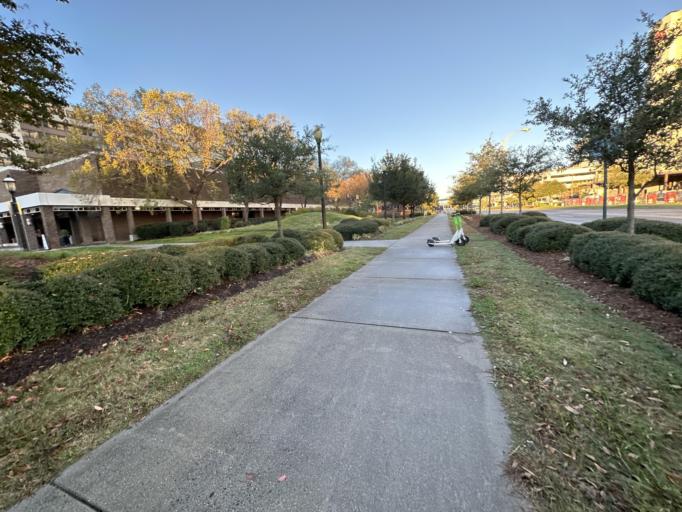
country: US
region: Virginia
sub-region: City of Norfolk
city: Norfolk
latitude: 36.8442
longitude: -76.2890
